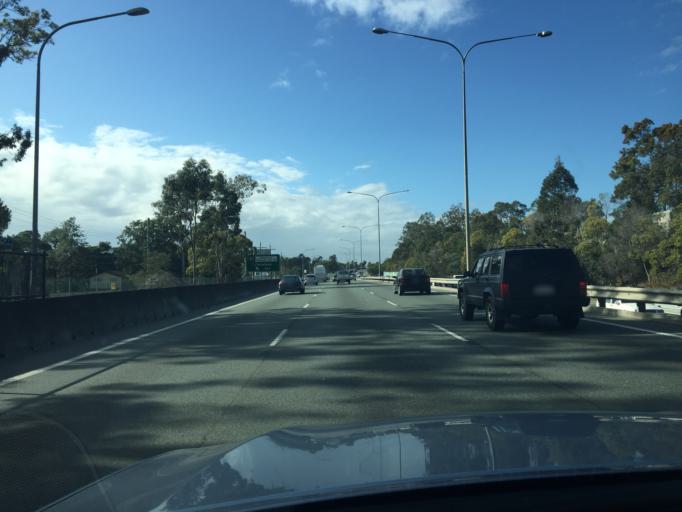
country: AU
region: Queensland
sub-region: Logan
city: Slacks Creek
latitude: -27.6716
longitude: 153.1802
